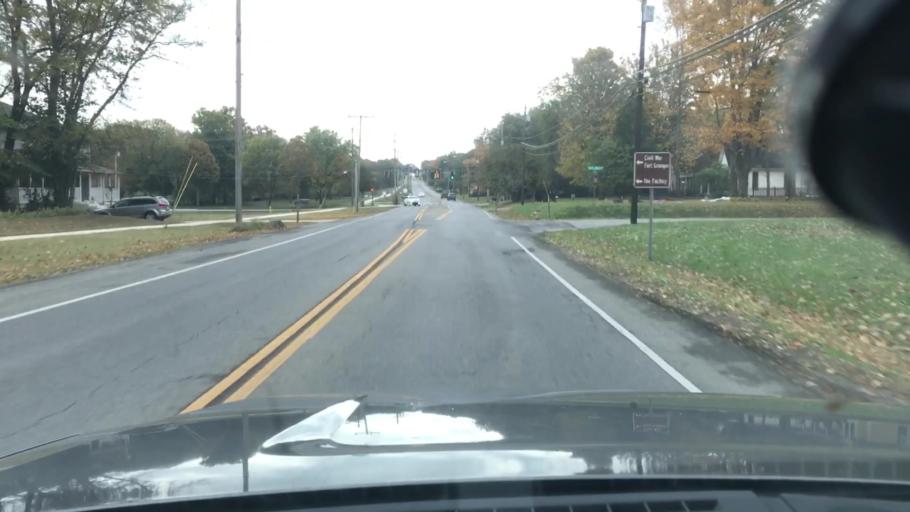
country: US
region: Tennessee
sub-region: Williamson County
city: Franklin
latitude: 35.9187
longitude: -86.8598
